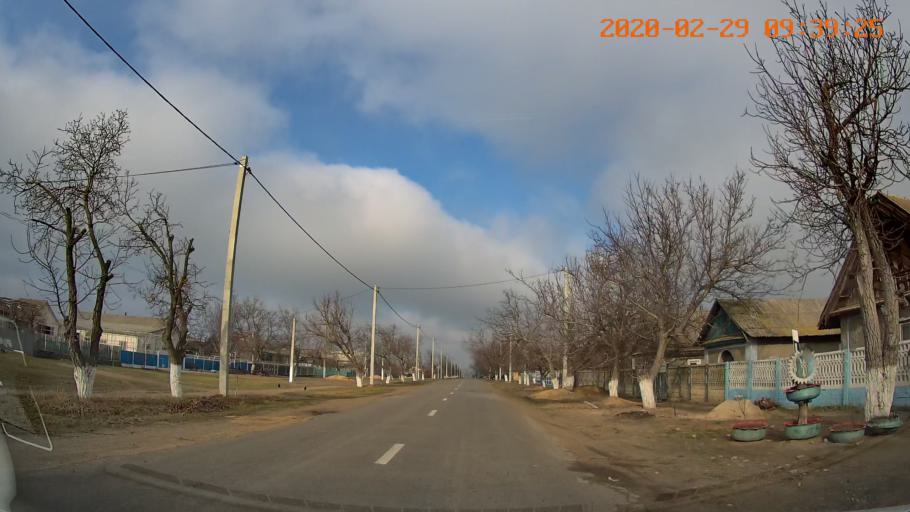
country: MD
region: Telenesti
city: Crasnoe
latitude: 46.6354
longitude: 29.8550
